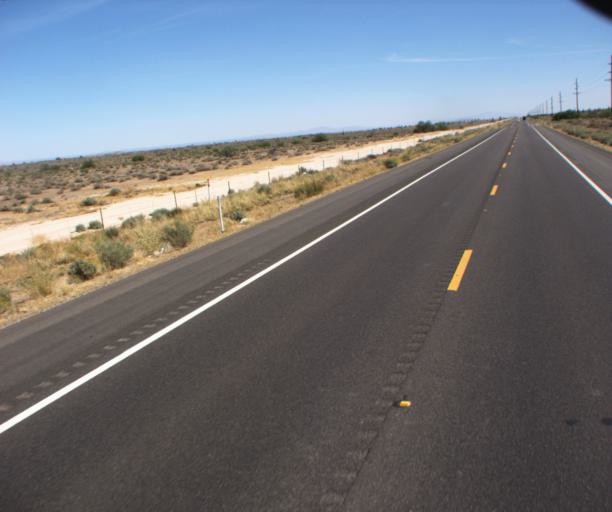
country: US
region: Arizona
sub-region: Pinal County
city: Blackwater
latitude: 33.0386
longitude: -111.6588
